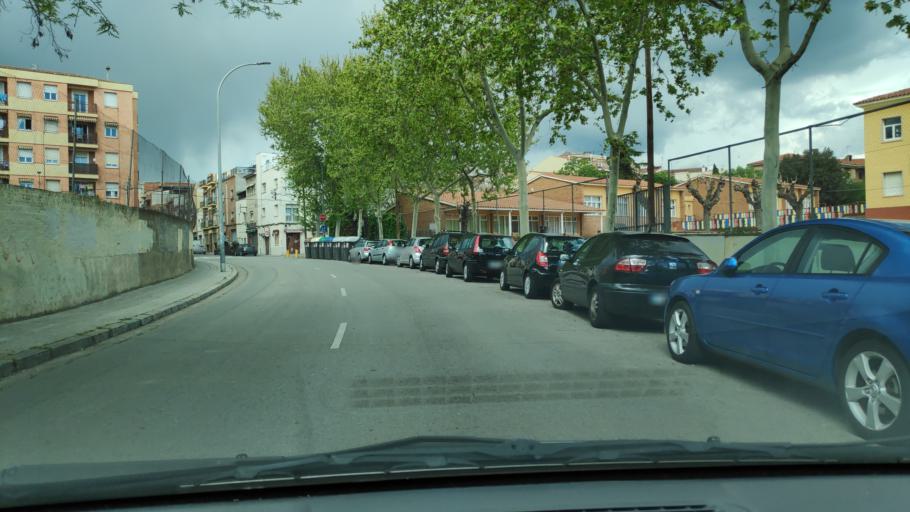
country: ES
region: Catalonia
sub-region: Provincia de Barcelona
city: Sabadell
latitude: 41.5638
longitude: 2.0923
